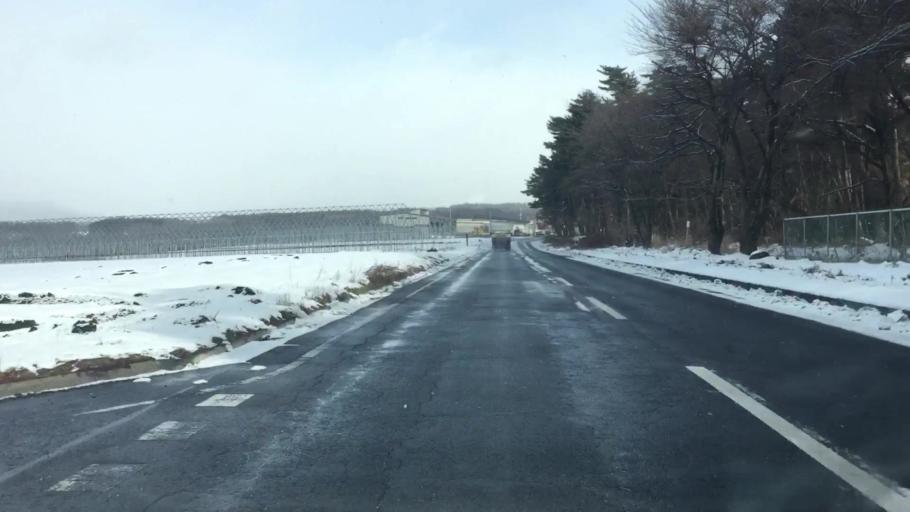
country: JP
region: Gunma
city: Numata
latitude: 36.6241
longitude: 139.0899
